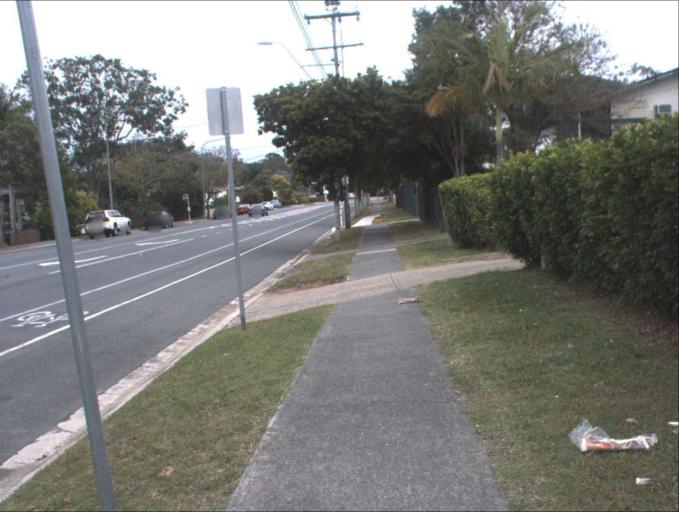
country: AU
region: Queensland
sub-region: Logan
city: Logan City
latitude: -27.6508
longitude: 153.1102
